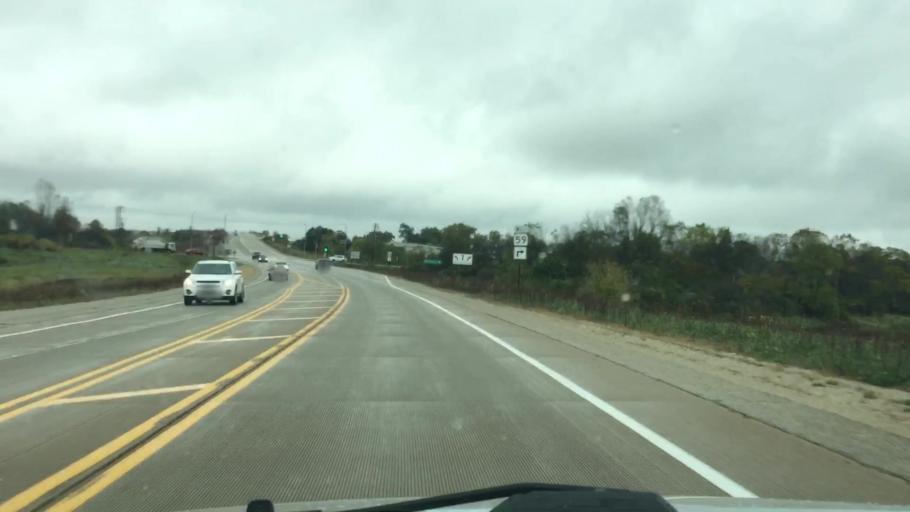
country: US
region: Wisconsin
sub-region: Walworth County
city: Whitewater
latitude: 42.8199
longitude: -88.7425
